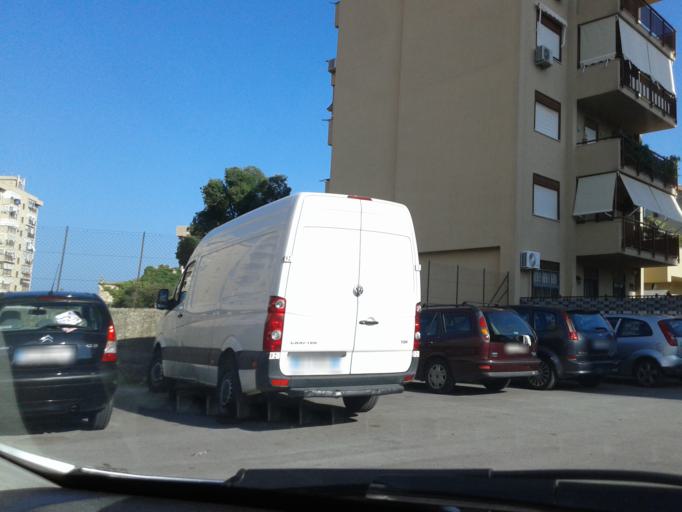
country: IT
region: Sicily
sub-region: Palermo
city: Palermo
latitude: 38.1027
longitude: 13.3217
